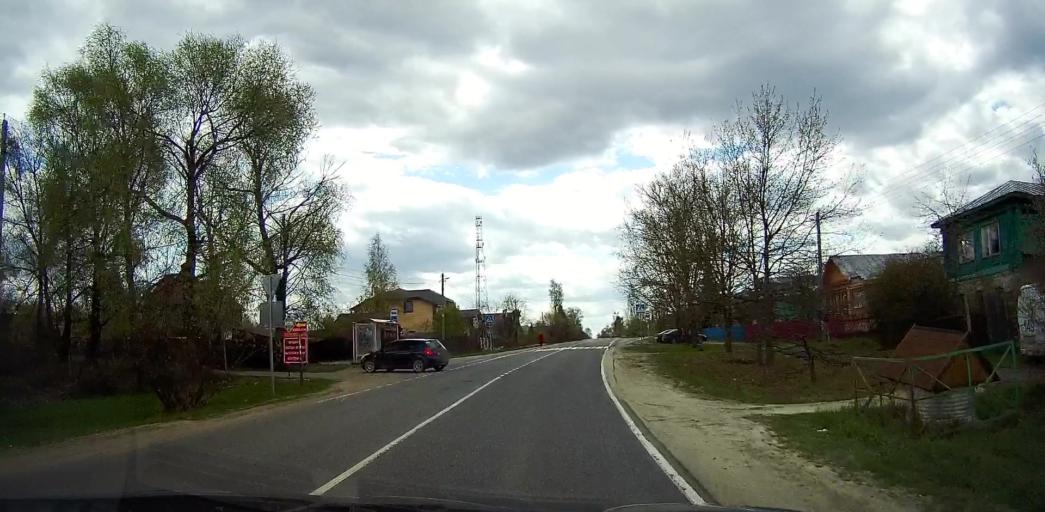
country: RU
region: Moskovskaya
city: Drezna
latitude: 55.6709
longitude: 38.7670
